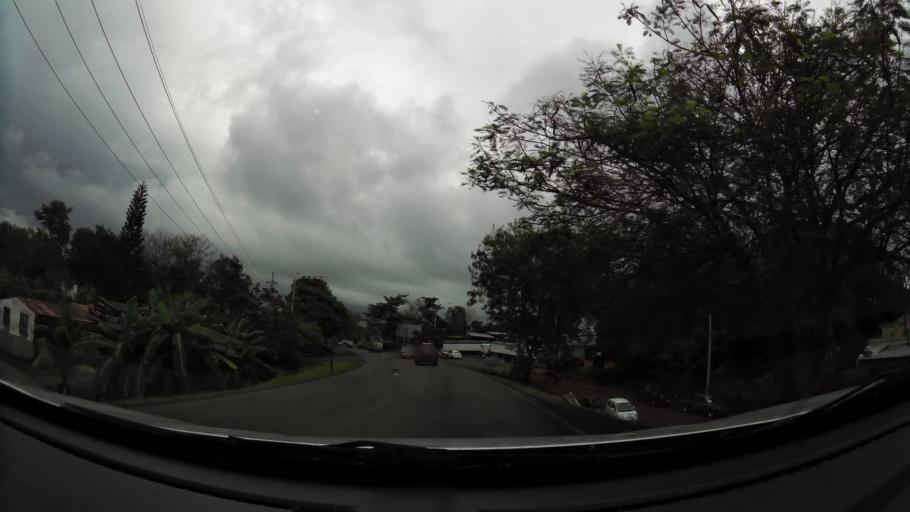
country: CR
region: Puntarenas
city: Esparza
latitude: 9.9954
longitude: -84.6725
